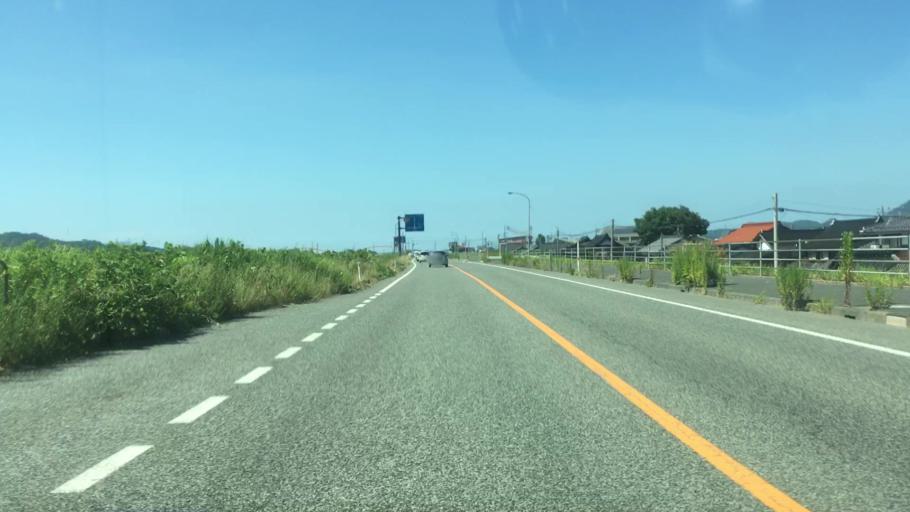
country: JP
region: Tottori
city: Tottori
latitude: 35.4610
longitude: 134.2151
